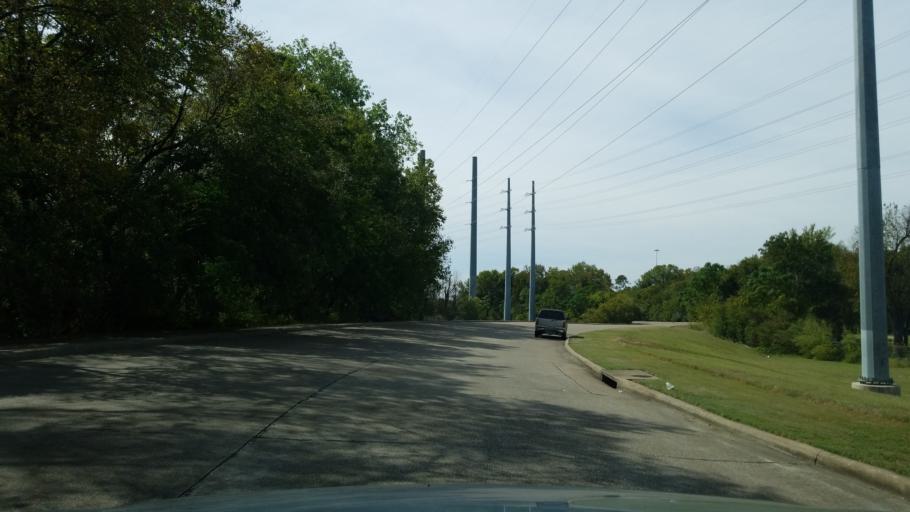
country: US
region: Texas
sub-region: Dallas County
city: Highland Park
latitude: 32.7951
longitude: -96.7259
